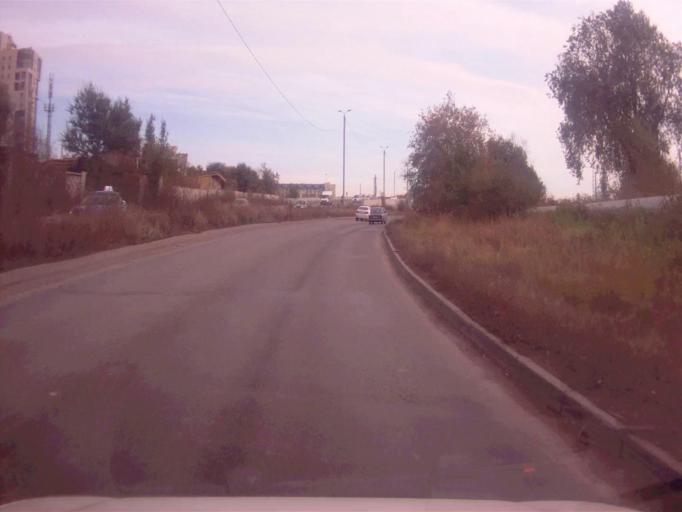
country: RU
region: Chelyabinsk
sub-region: Gorod Chelyabinsk
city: Chelyabinsk
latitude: 55.1588
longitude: 61.4372
